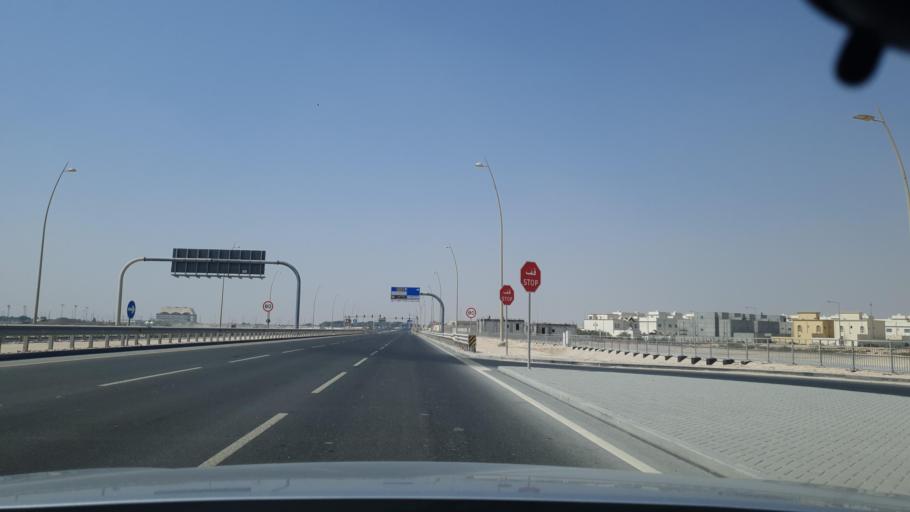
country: QA
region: Al Khawr
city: Al Khawr
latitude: 25.6628
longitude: 51.4959
